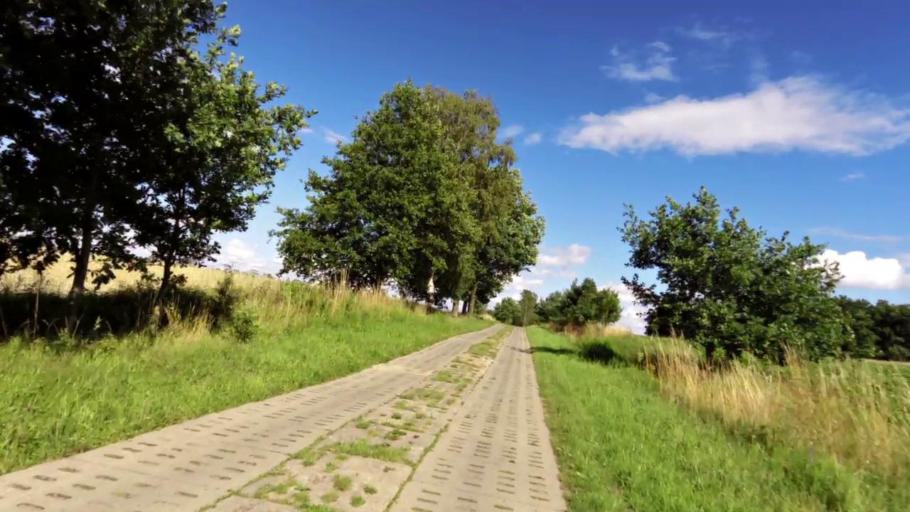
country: PL
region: West Pomeranian Voivodeship
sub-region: Powiat slawienski
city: Slawno
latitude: 54.4630
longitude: 16.7205
